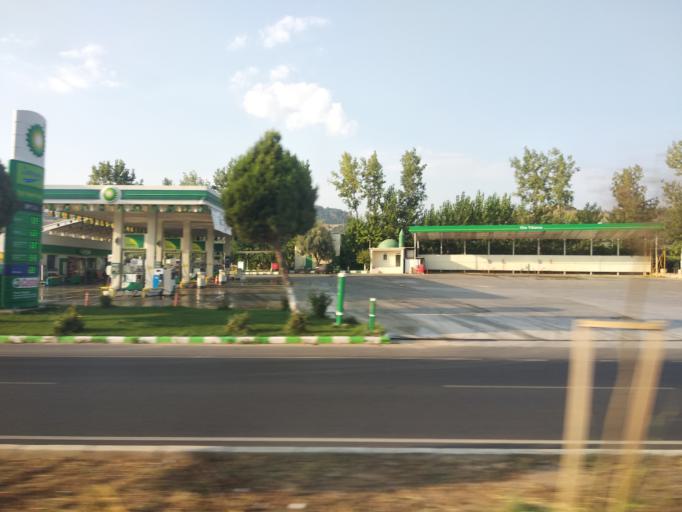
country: TR
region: Manisa
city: Ahmetli
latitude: 38.5073
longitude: 27.9912
